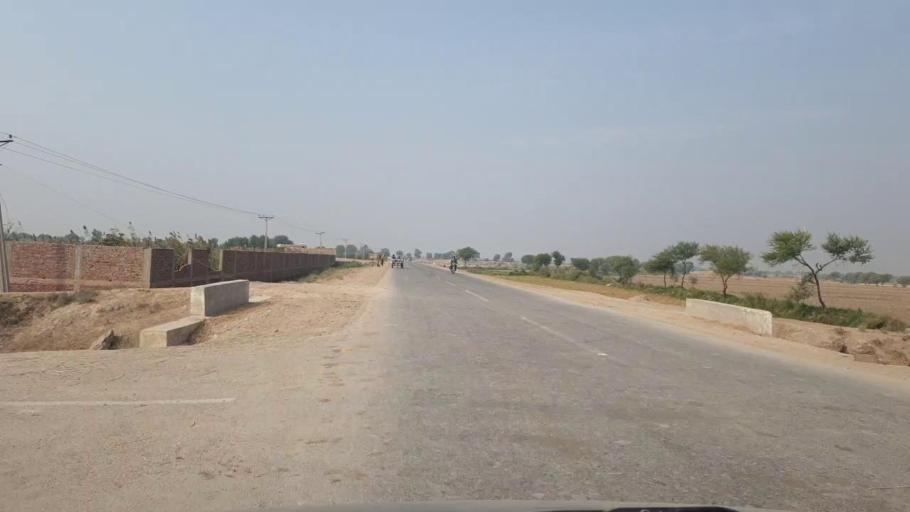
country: PK
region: Sindh
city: Tando Muhammad Khan
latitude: 25.1278
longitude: 68.4975
